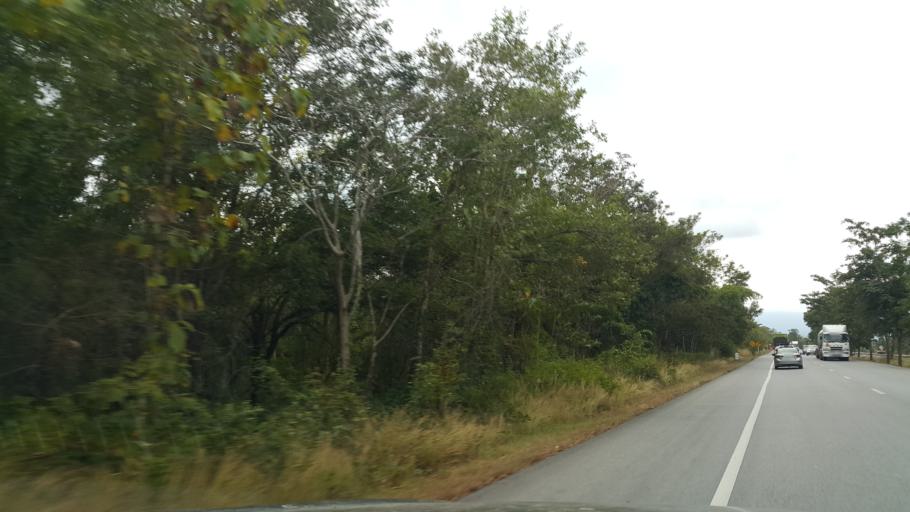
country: TH
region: Lampang
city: Sop Prap
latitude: 17.9793
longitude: 99.3558
